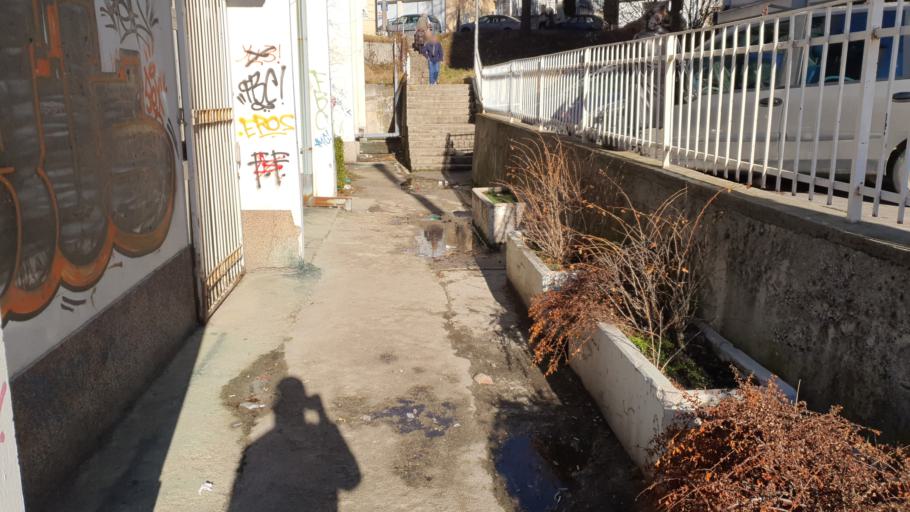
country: RS
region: Central Serbia
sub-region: Zlatiborski Okrug
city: Uzice
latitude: 43.8585
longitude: 19.8409
